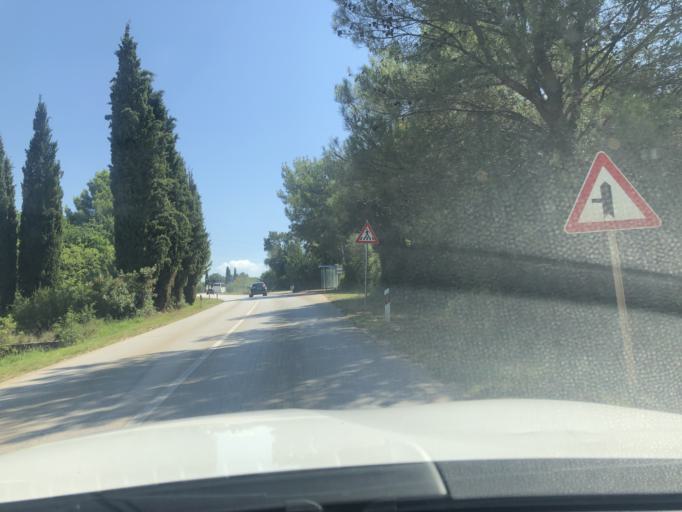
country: HR
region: Istarska
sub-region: Grad Rovinj
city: Rovinj
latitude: 45.0566
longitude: 13.7061
